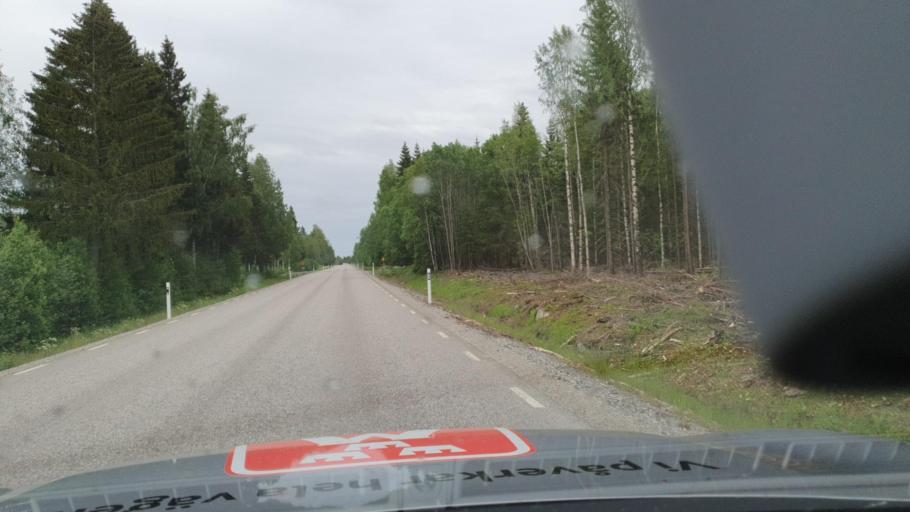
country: SE
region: Vaesternorrland
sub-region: Kramfors Kommun
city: Kramfors
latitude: 62.9216
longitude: 17.9402
